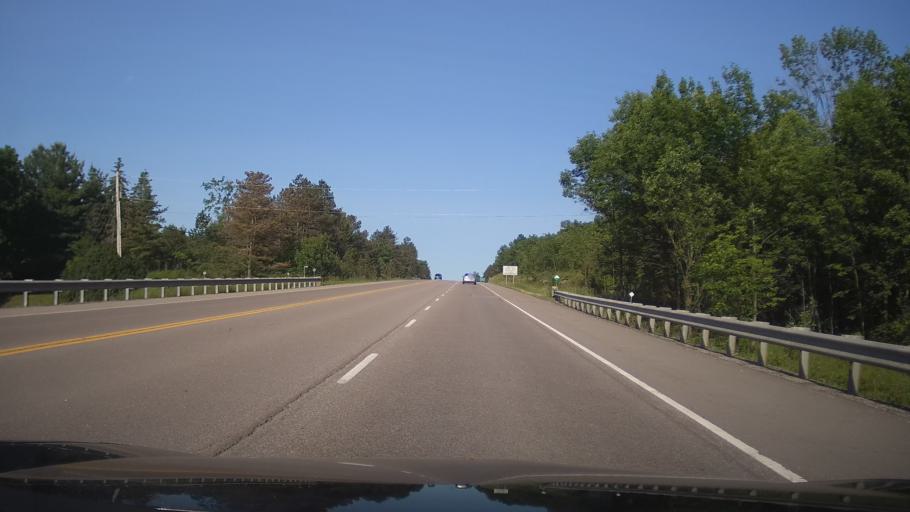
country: CA
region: Ontario
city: Quinte West
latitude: 44.4914
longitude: -77.6521
